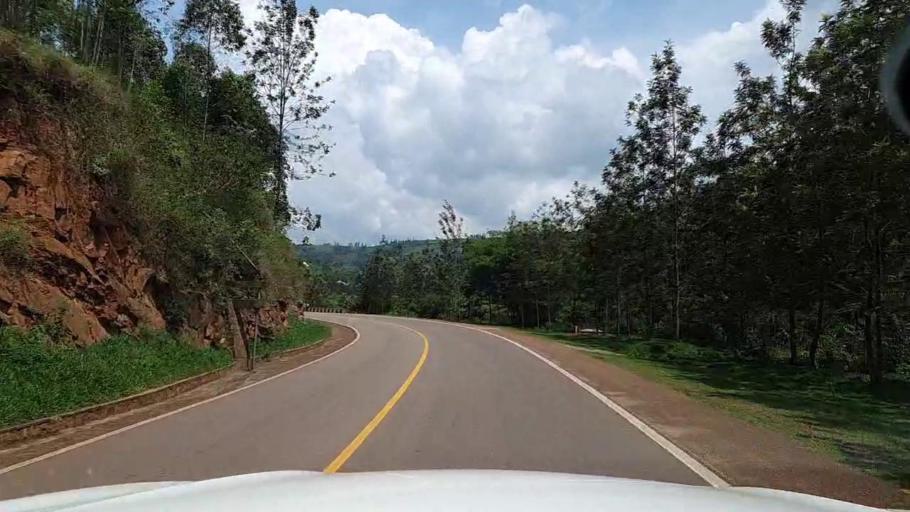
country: RW
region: Kigali
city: Kigali
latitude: -1.8305
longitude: 30.0788
